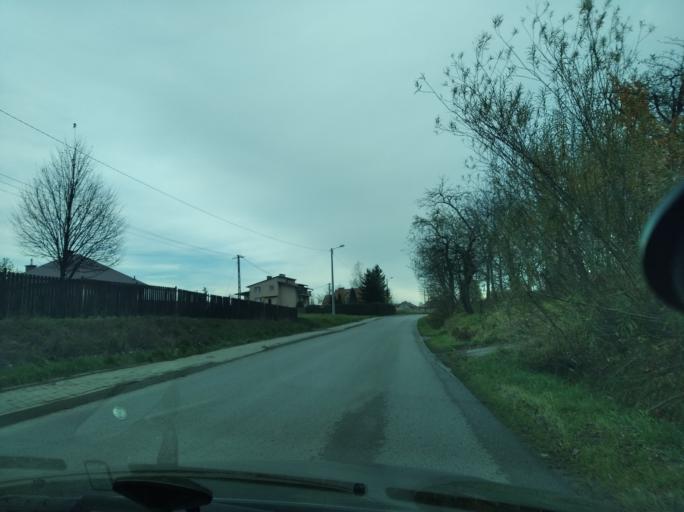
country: PL
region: Subcarpathian Voivodeship
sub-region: Powiat lancucki
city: Albigowa
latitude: 50.0325
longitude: 22.2365
